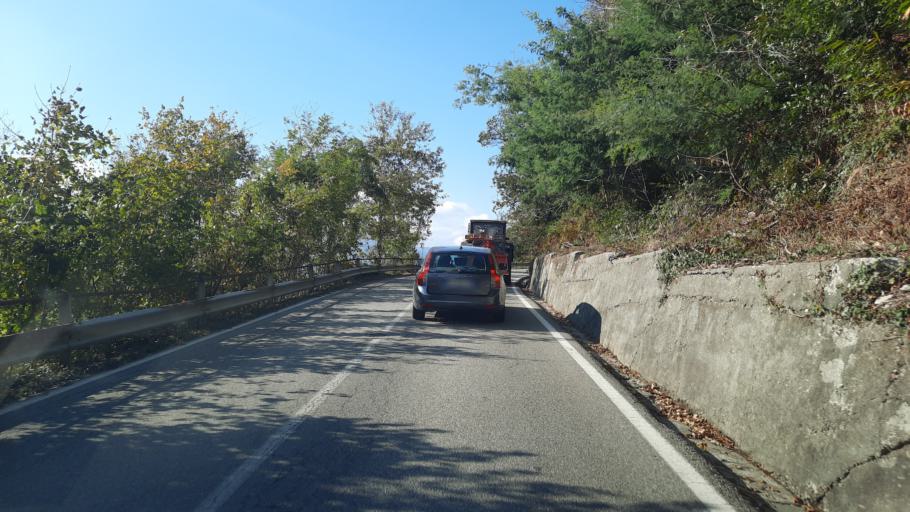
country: IT
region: Piedmont
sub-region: Provincia di Novara
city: Bolzano Novarese
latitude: 45.7722
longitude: 8.4395
